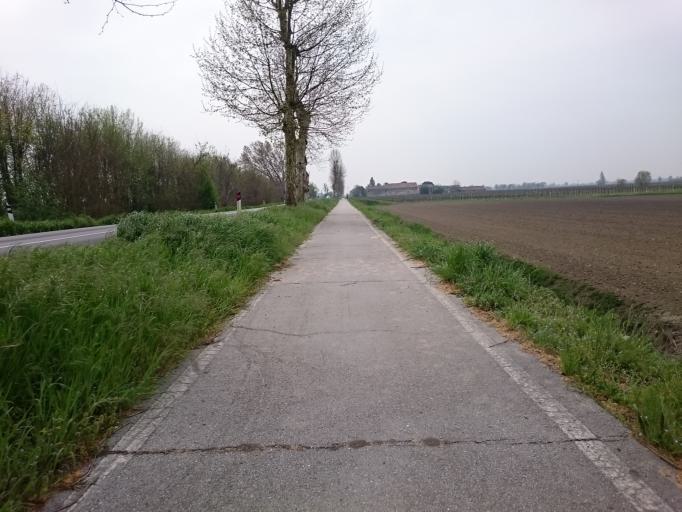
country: IT
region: Veneto
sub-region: Provincia di Padova
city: Bagnoli di Sopra
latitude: 45.1687
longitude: 11.8786
